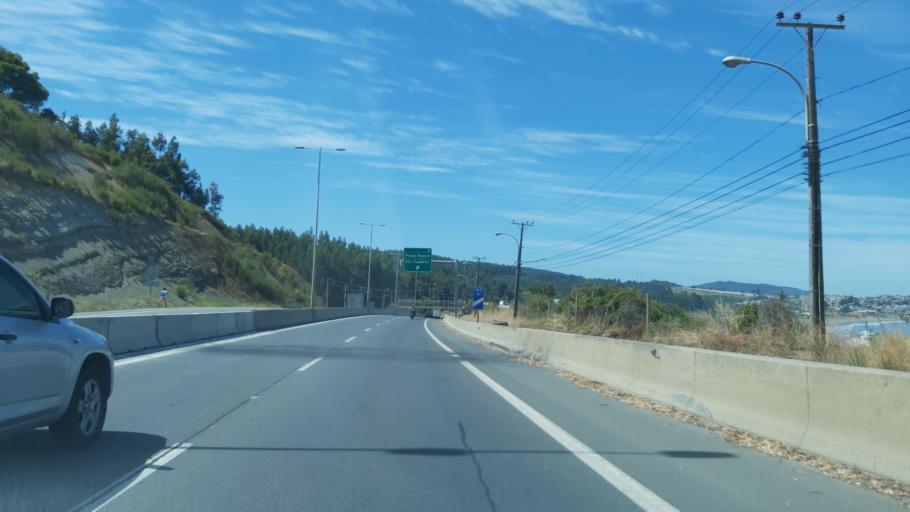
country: CL
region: Biobio
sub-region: Provincia de Concepcion
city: Coronel
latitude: -37.0534
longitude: -73.1408
